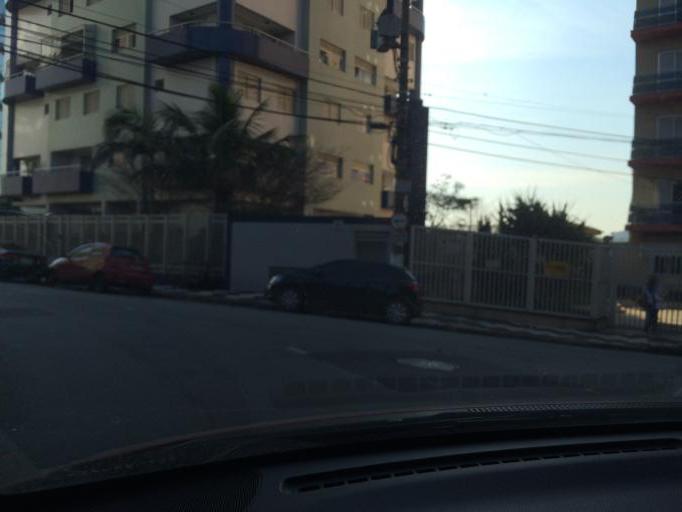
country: BR
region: Sao Paulo
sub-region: Osasco
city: Osasco
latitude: -23.5404
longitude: -46.7751
